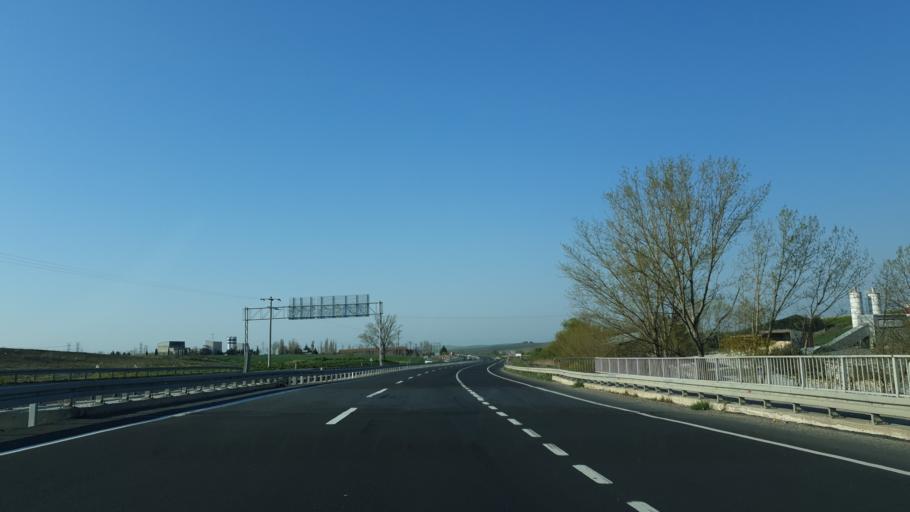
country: TR
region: Tekirdag
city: Corlu
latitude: 41.1249
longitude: 27.7541
